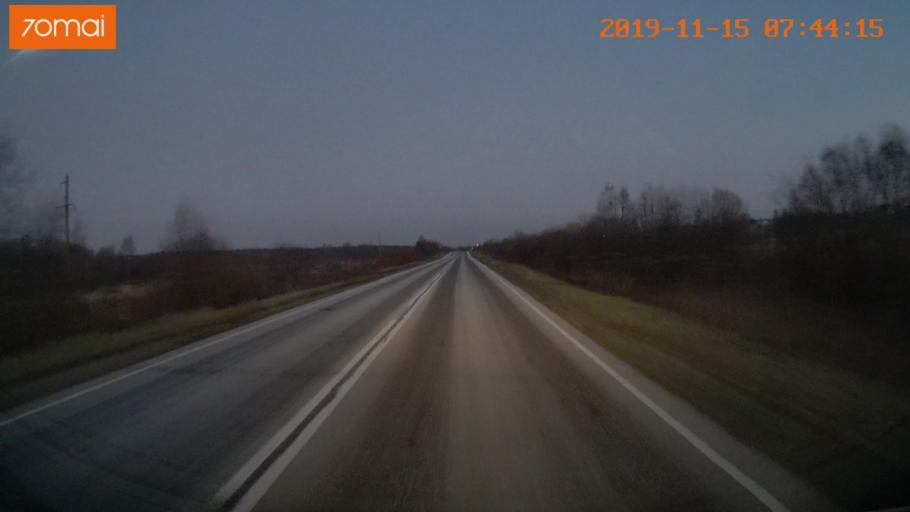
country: RU
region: Vologda
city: Sheksna
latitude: 58.8115
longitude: 38.3157
